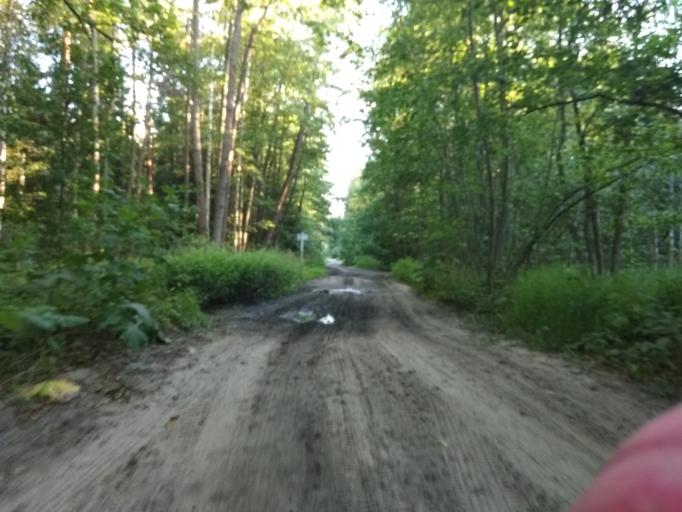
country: RU
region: Moskovskaya
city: Misheronskiy
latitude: 55.7299
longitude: 39.7612
